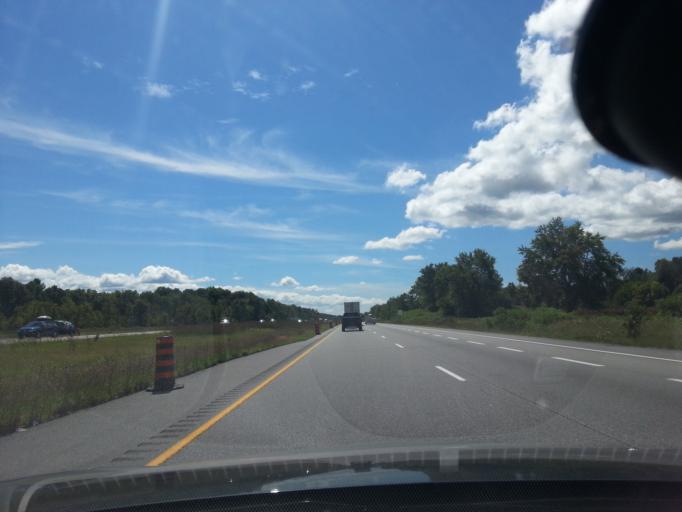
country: US
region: New York
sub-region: Jefferson County
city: Alexandria Bay
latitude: 44.4733
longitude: -75.8705
